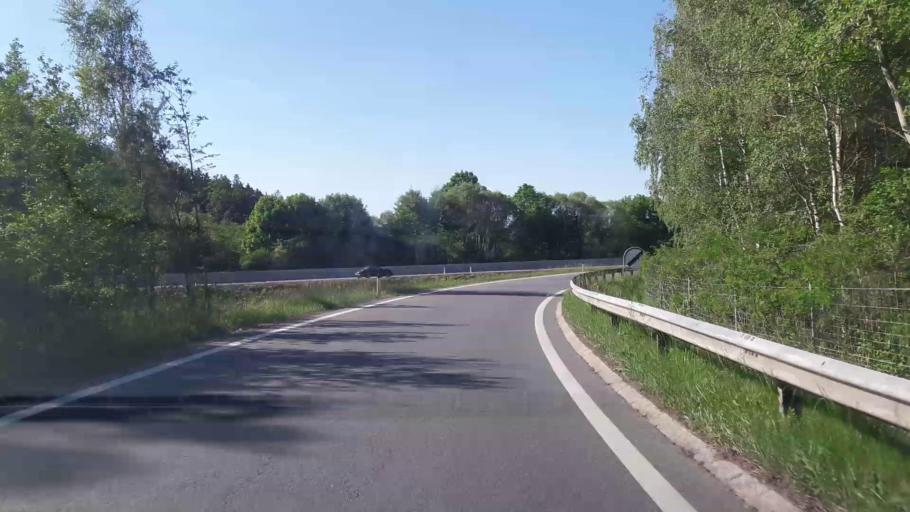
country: AT
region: Burgenland
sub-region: Politischer Bezirk Oberwart
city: Markt Allhau
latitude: 47.2819
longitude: 16.0641
